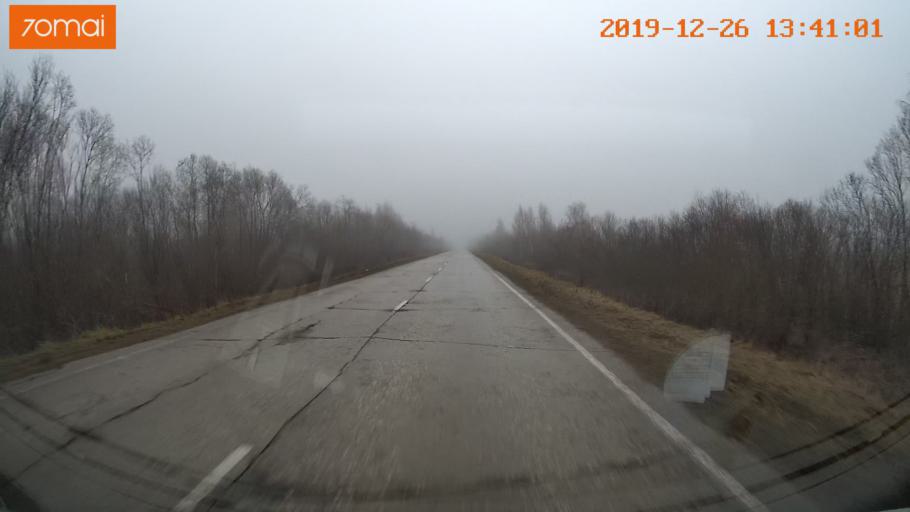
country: RU
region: Vologda
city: Sheksna
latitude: 58.7359
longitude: 38.4410
